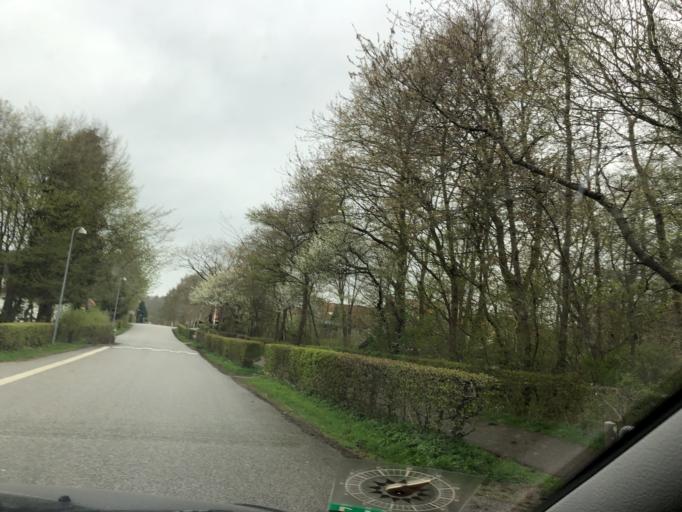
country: DK
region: Zealand
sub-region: Lejre Kommune
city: Kirke Hvalso
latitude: 55.5224
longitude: 11.8612
